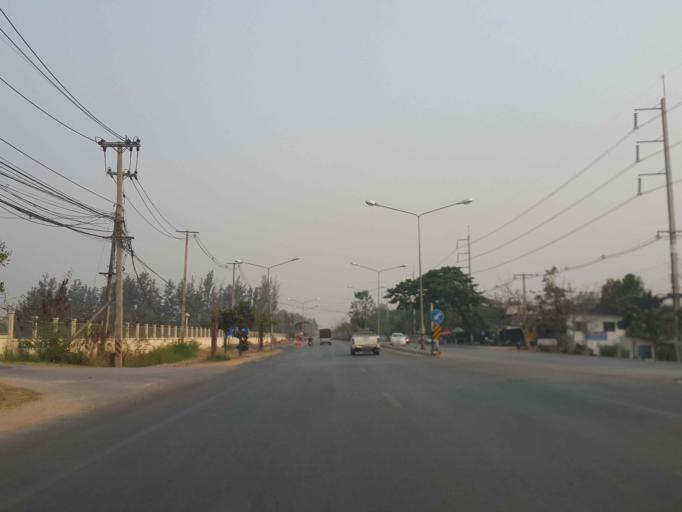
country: TH
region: Chiang Mai
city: San Sai
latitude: 18.9097
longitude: 99.0010
